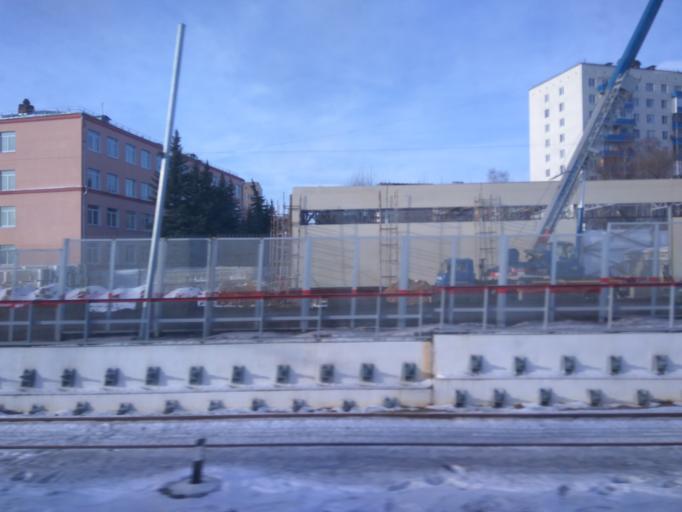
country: RU
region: Moskovskaya
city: Bogorodskoye
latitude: 55.7991
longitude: 37.7461
